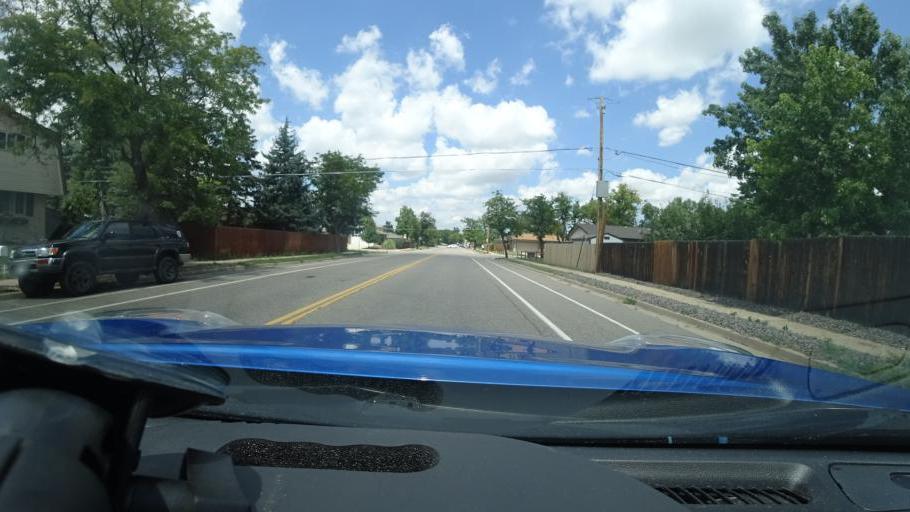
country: US
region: Colorado
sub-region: Adams County
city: Aurora
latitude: 39.7038
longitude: -104.8388
